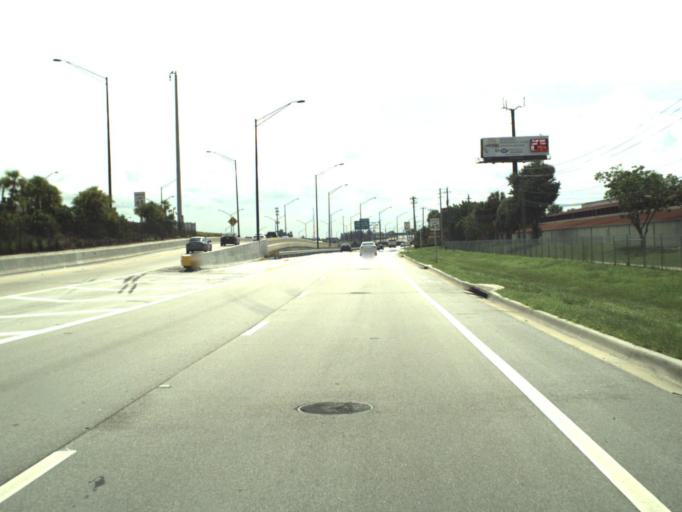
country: US
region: Florida
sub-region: Broward County
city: Pine Island Ridge
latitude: 26.1173
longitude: -80.3284
